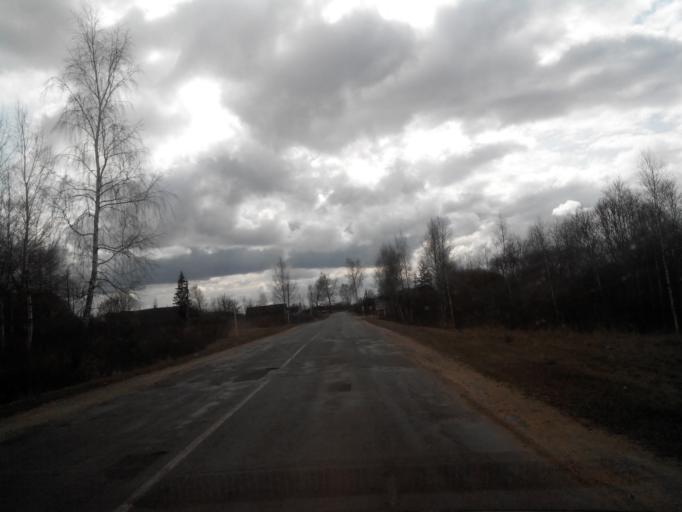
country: BY
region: Vitebsk
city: Pastavy
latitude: 55.1273
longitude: 26.9338
